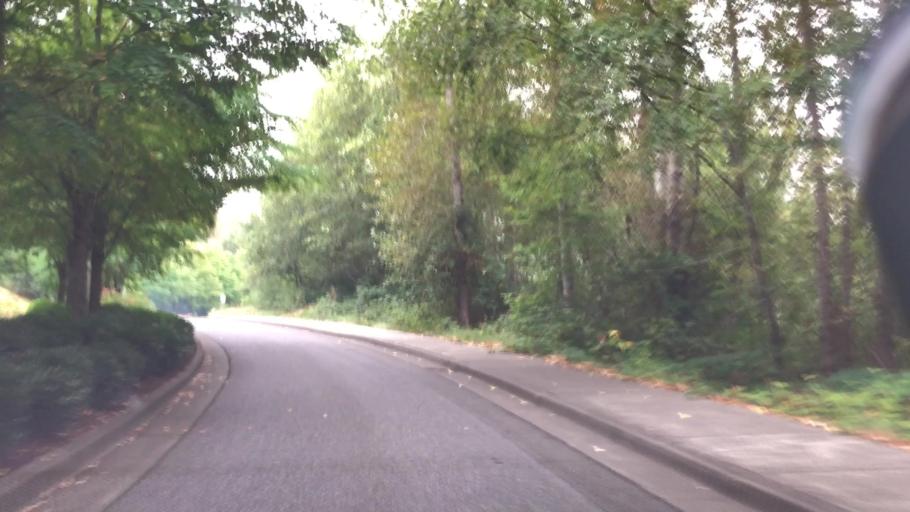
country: US
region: Washington
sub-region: Snohomish County
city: North Creek
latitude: 47.8017
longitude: -122.1978
